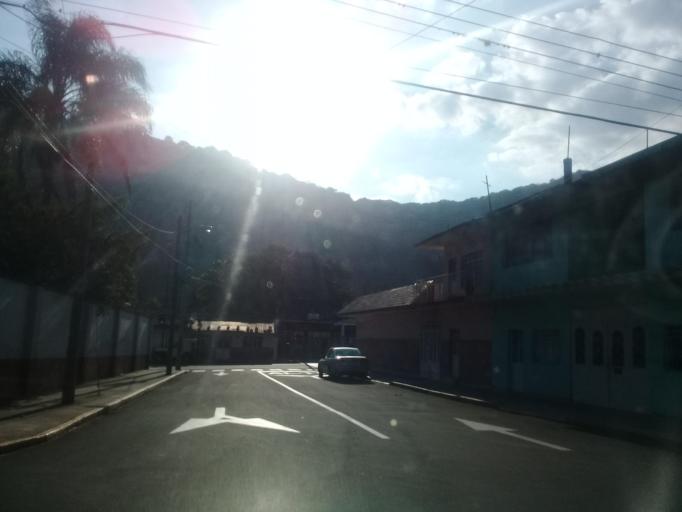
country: MX
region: Veracruz
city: Orizaba
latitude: 18.8539
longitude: -97.1132
